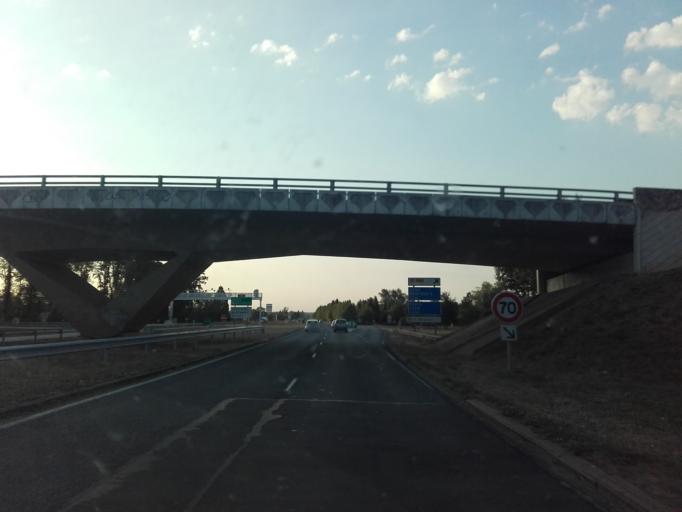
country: FR
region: Bourgogne
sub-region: Departement de l'Yonne
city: Gurgy
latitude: 47.8473
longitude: 3.5492
